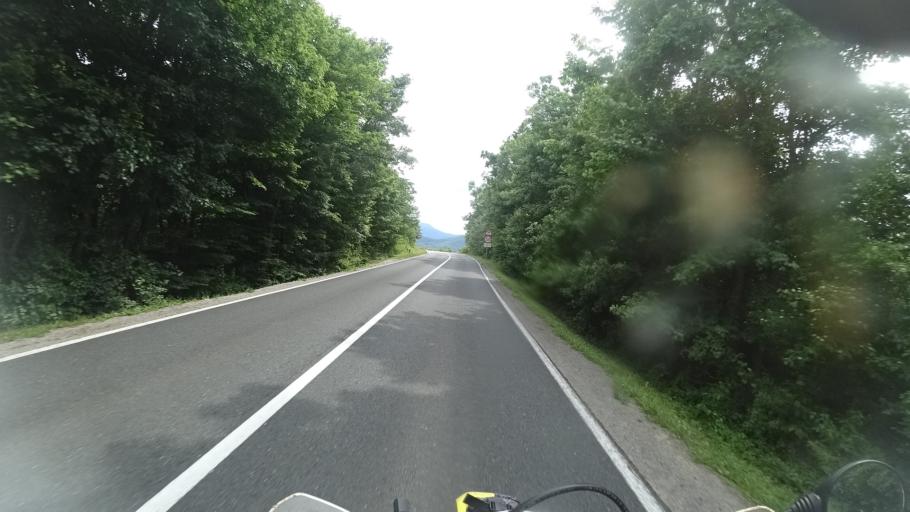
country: HR
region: Licko-Senjska
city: Jezerce
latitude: 44.9278
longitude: 15.7023
